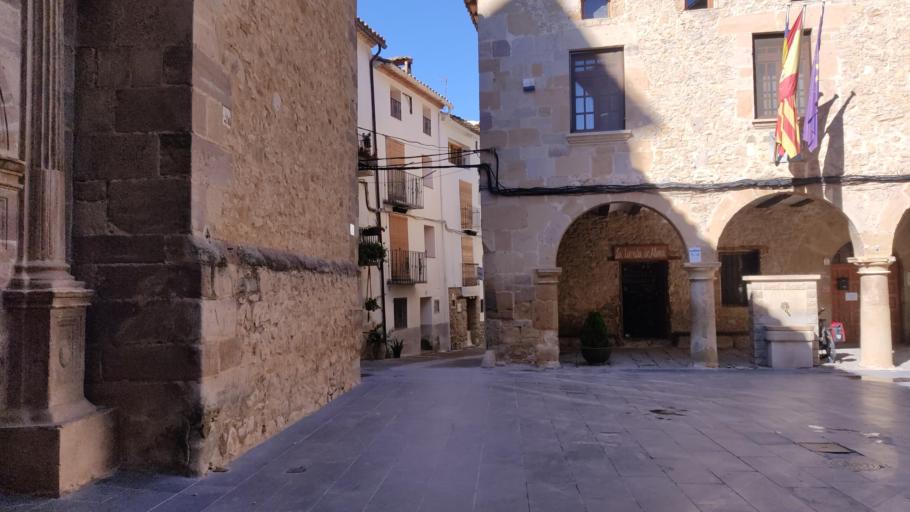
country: ES
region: Valencia
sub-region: Provincia de Castello
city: Puebla de Arenoso
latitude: 40.1046
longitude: -0.5907
